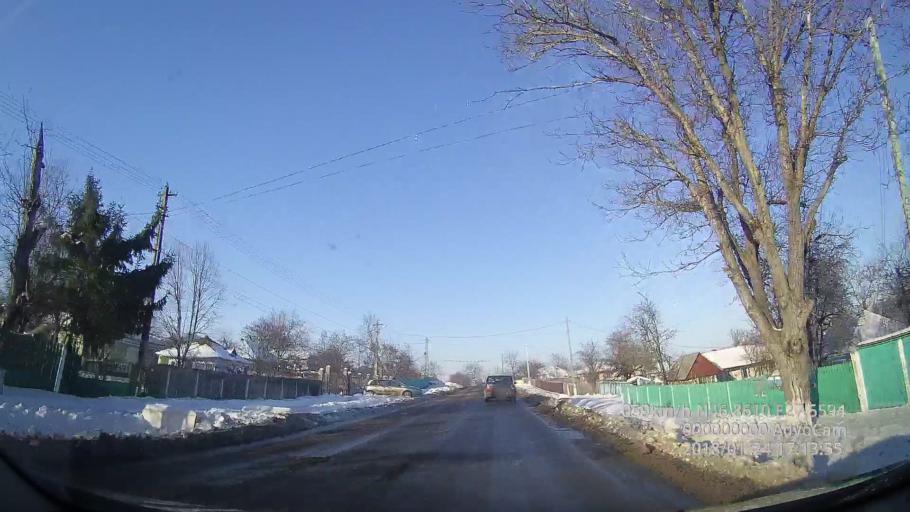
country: RO
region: Vaslui
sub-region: Comuna Rebricea
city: Rebricea
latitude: 46.8615
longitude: 27.5594
